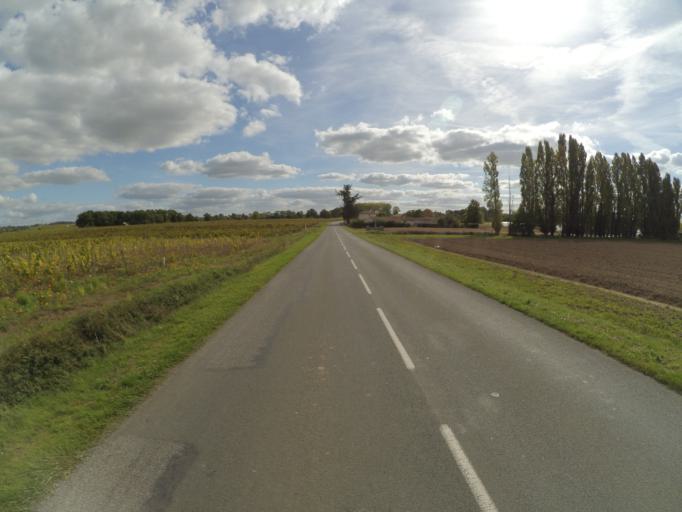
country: FR
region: Pays de la Loire
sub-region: Departement de la Loire-Atlantique
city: Le Loroux-Bottereau
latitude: 47.2077
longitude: -1.3494
